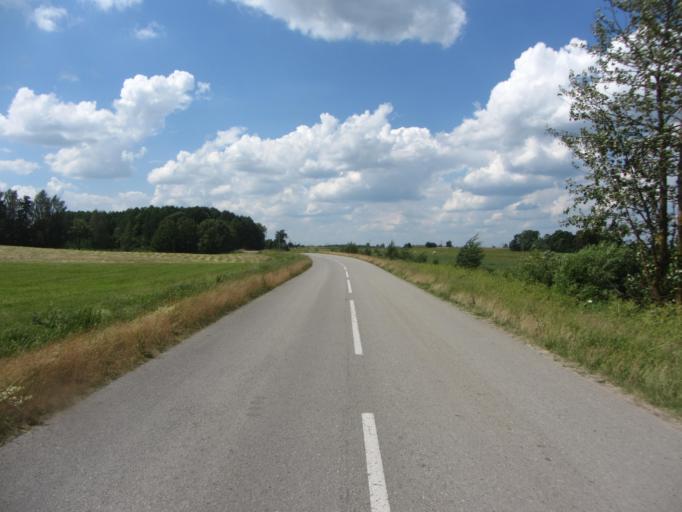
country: LT
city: Jieznas
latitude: 54.4820
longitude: 24.1961
